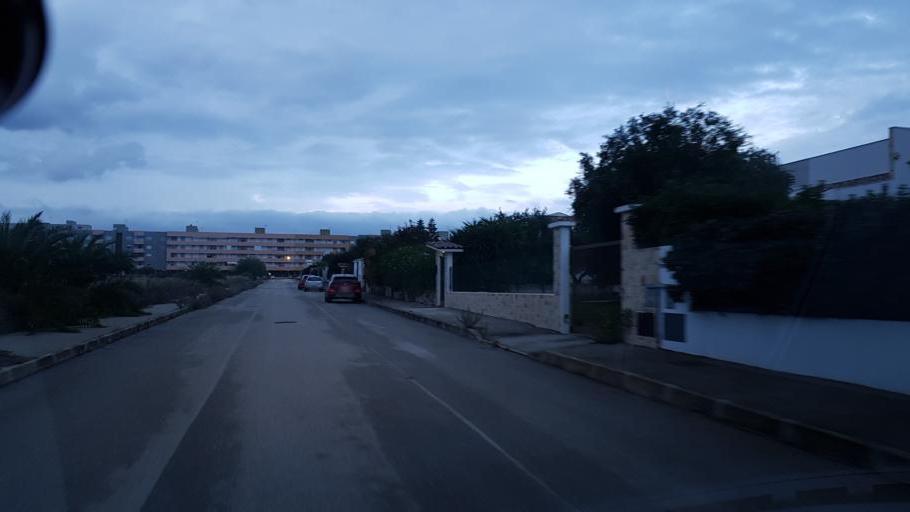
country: IT
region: Apulia
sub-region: Provincia di Taranto
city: Paolo VI
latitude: 40.5290
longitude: 17.2848
